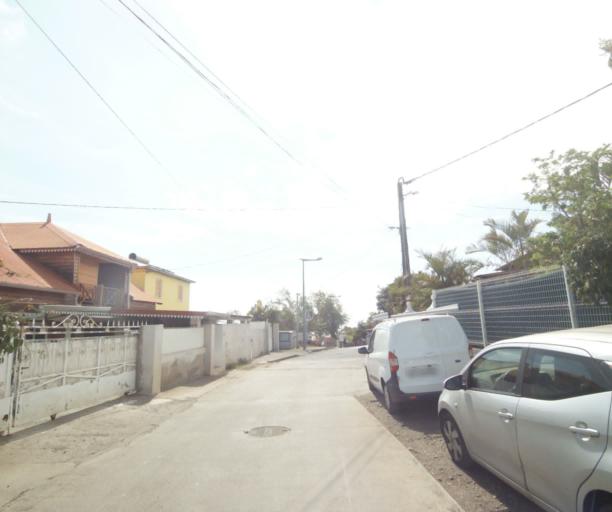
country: RE
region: Reunion
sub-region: Reunion
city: Saint-Paul
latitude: -21.0512
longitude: 55.2645
